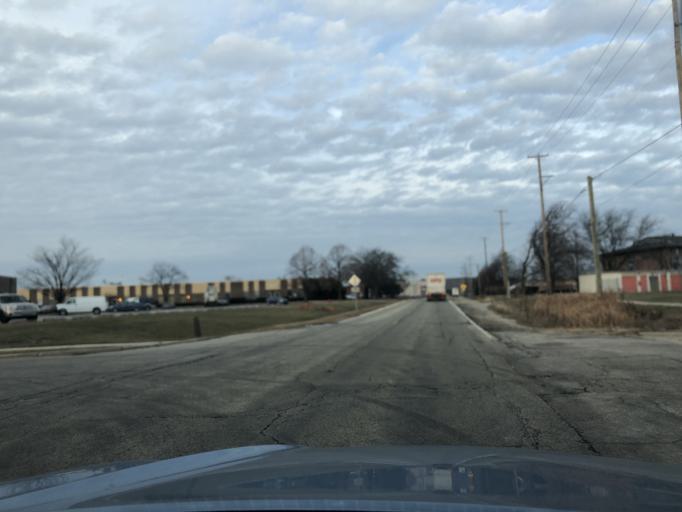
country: US
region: Illinois
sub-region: Cook County
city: Elk Grove Village
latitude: 42.0062
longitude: -87.9363
